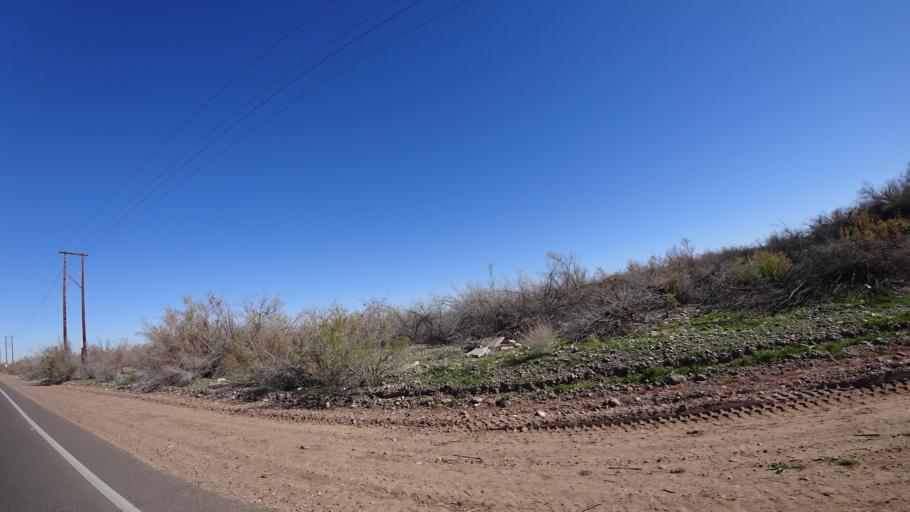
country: US
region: Arizona
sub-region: Maricopa County
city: Tolleson
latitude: 33.3817
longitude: -112.2543
